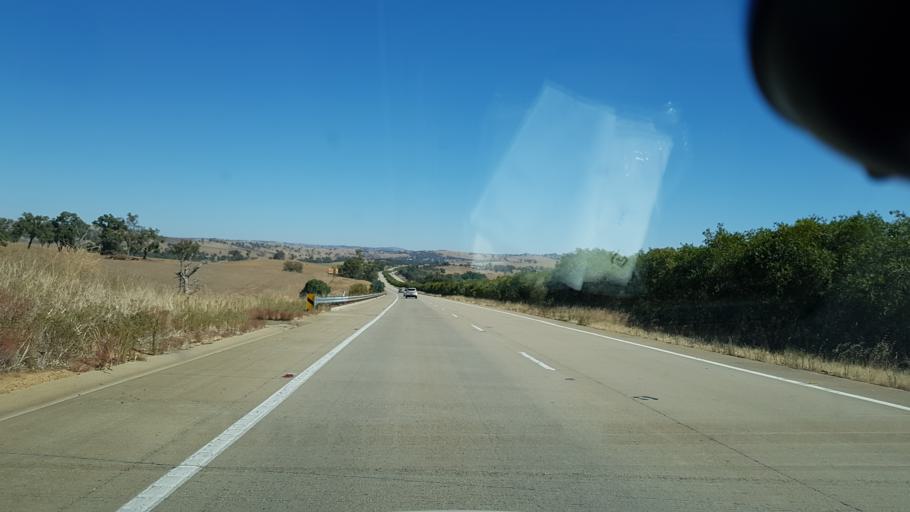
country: AU
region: New South Wales
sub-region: Gundagai
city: Gundagai
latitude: -34.8166
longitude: 148.3947
